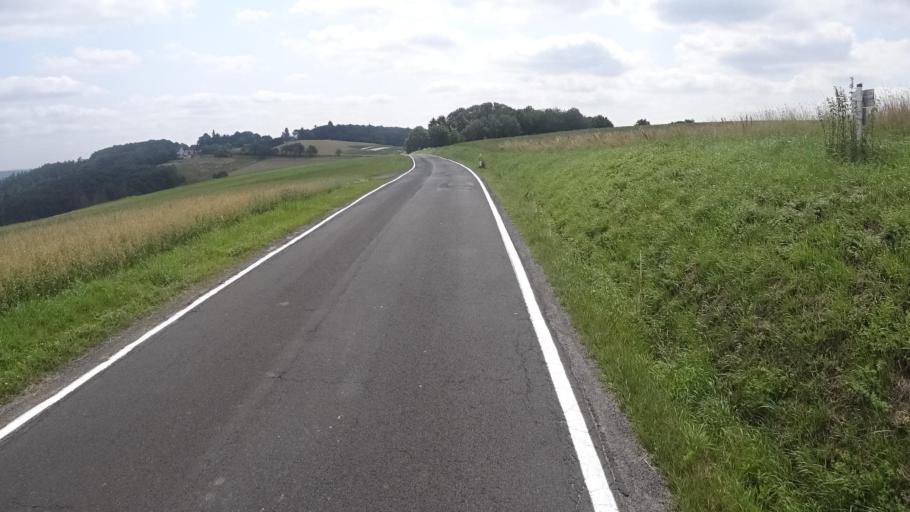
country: DE
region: Rheinland-Pfalz
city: Sankt Katharinen
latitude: 50.5881
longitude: 7.3565
